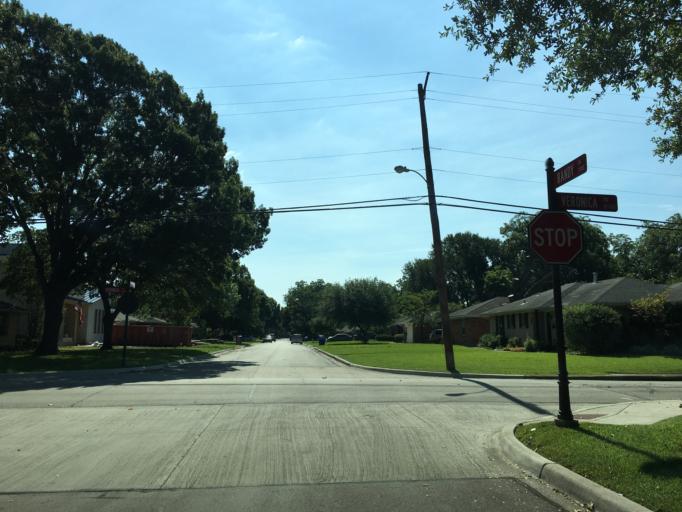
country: US
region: Texas
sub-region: Dallas County
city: Farmers Branch
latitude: 32.9210
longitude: -96.8794
